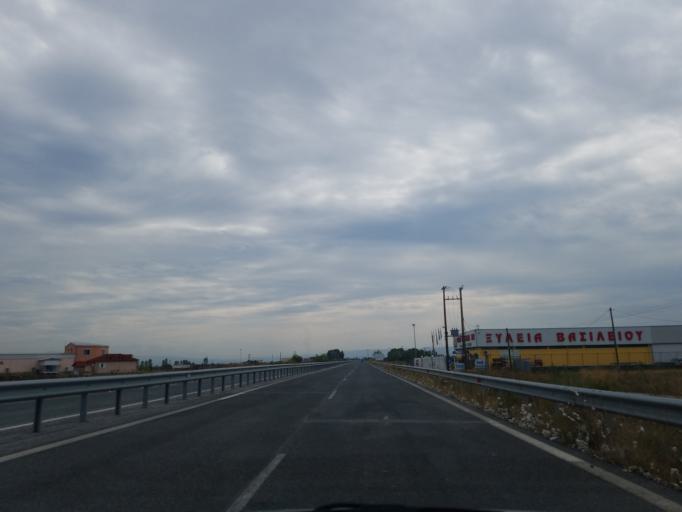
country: GR
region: Thessaly
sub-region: Nomos Kardhitsas
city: Sofades
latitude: 39.3187
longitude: 22.1126
